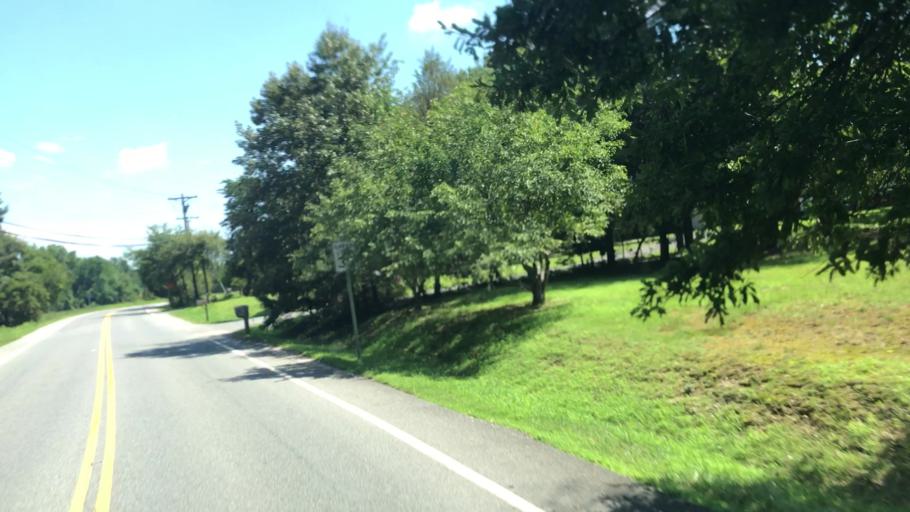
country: US
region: Maryland
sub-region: Prince George's County
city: Brandywine
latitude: 38.7120
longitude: -76.8845
